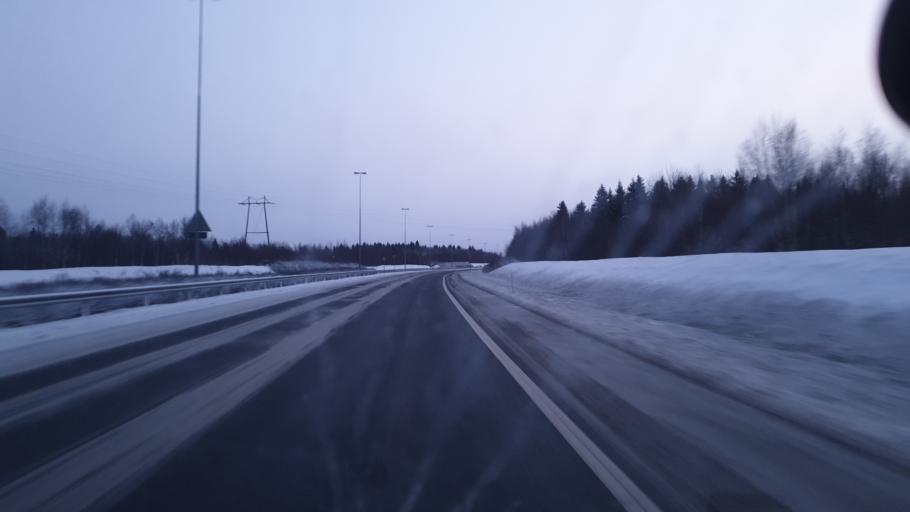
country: FI
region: Lapland
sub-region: Kemi-Tornio
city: Tornio
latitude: 65.8375
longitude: 24.2339
